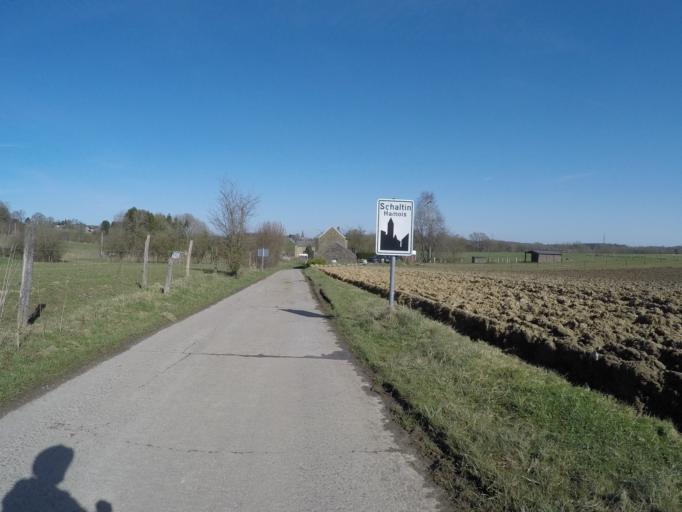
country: BE
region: Wallonia
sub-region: Province de Namur
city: Hamois
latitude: 50.3544
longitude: 5.1156
